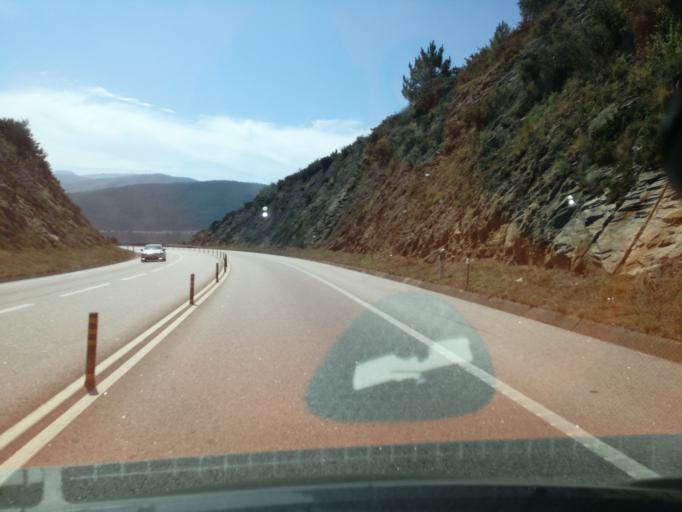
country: PT
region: Viana do Castelo
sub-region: Vila Nova de Cerveira
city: Vila Nova de Cerveira
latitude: 41.8987
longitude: -8.7868
